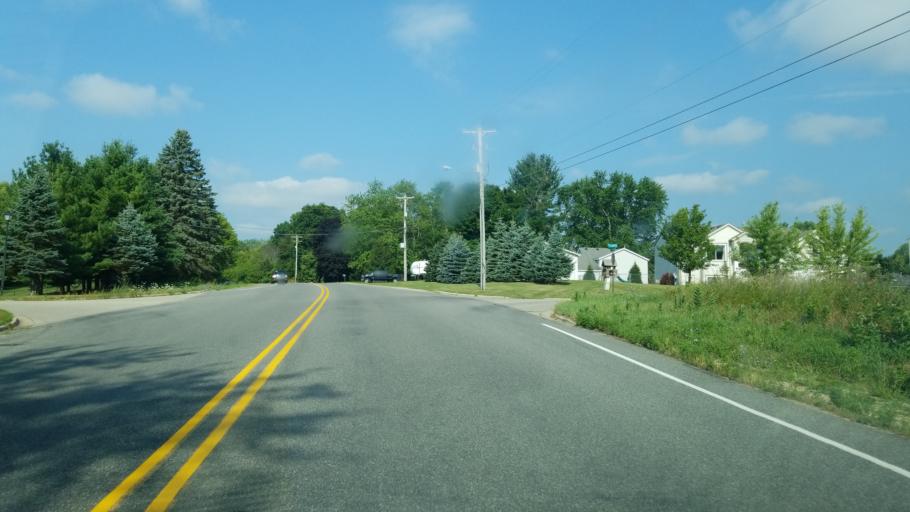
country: US
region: Michigan
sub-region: Kent County
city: Comstock Park
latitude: 43.0904
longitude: -85.6453
